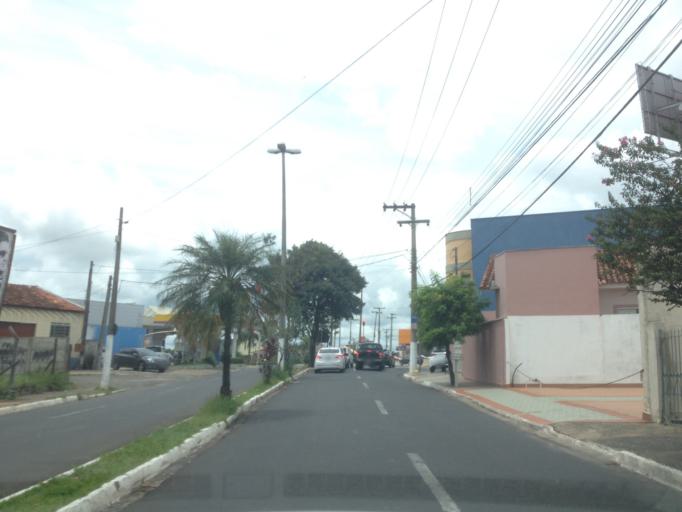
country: BR
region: Sao Paulo
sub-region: Marilia
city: Marilia
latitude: -22.2283
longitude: -49.9308
